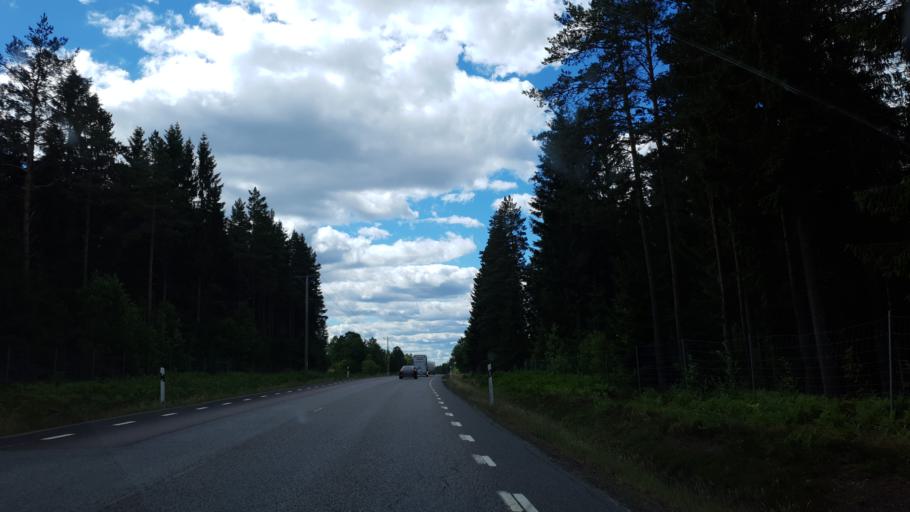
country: SE
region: Kronoberg
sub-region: Vaxjo Kommun
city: Braas
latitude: 57.1631
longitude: 15.1624
